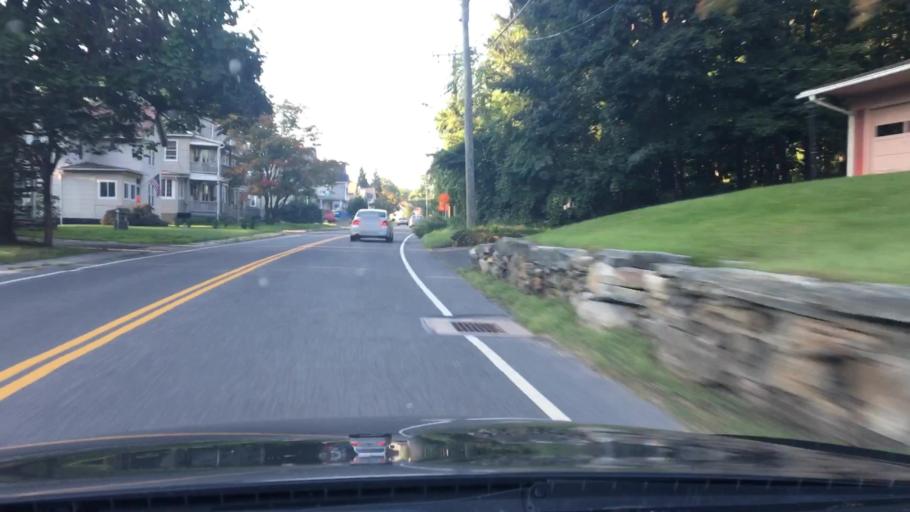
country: US
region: Connecticut
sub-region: Litchfield County
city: New Milford
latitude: 41.5708
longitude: -73.4069
